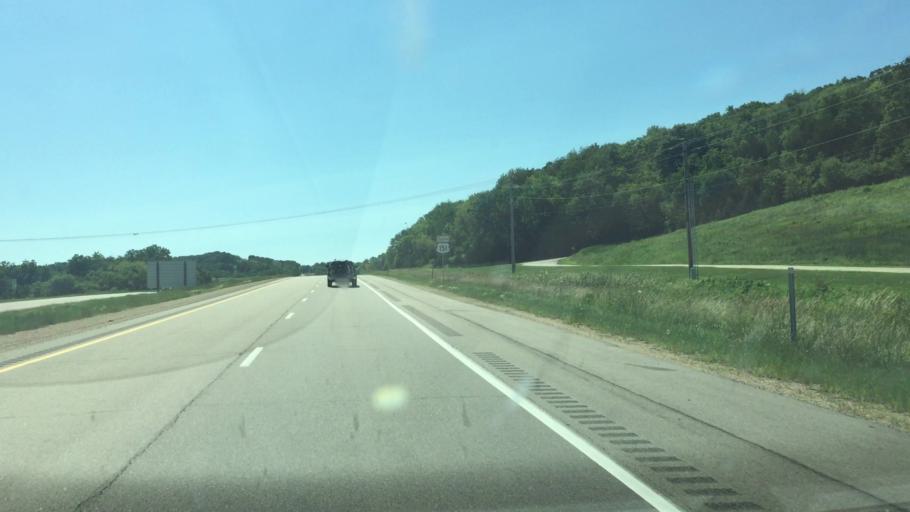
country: US
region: Iowa
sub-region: Dubuque County
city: Dubuque
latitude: 42.4190
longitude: -90.7008
